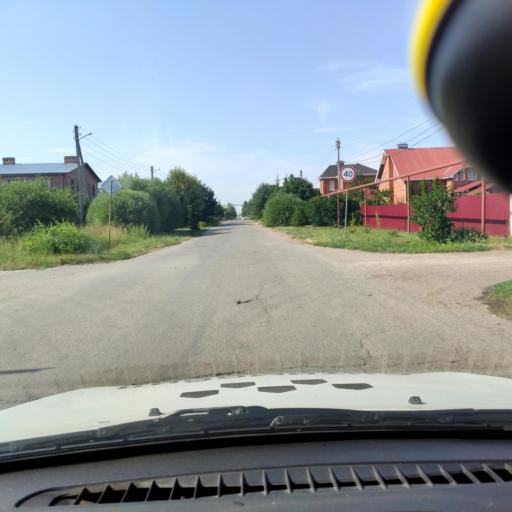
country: RU
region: Samara
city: Podstepki
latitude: 53.5160
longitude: 49.1815
